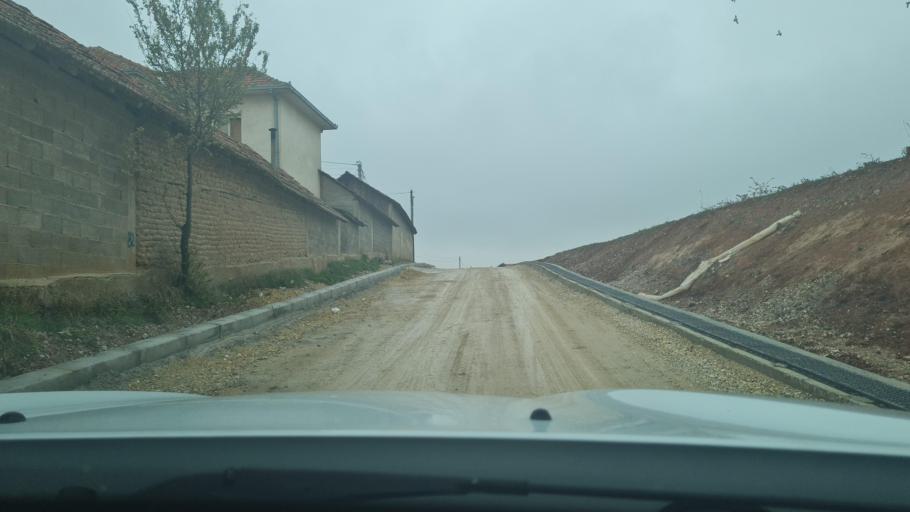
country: MK
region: Opstina Lipkovo
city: Matejche
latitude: 42.1113
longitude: 21.6144
